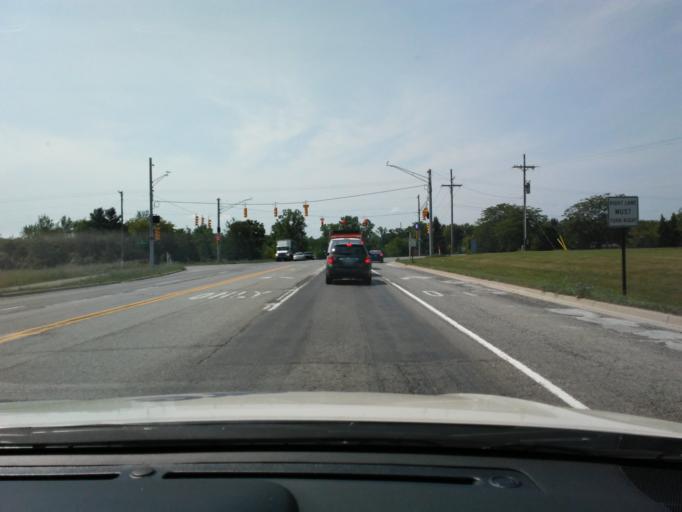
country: US
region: Michigan
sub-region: Oakland County
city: South Lyon
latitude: 42.5187
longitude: -83.6896
